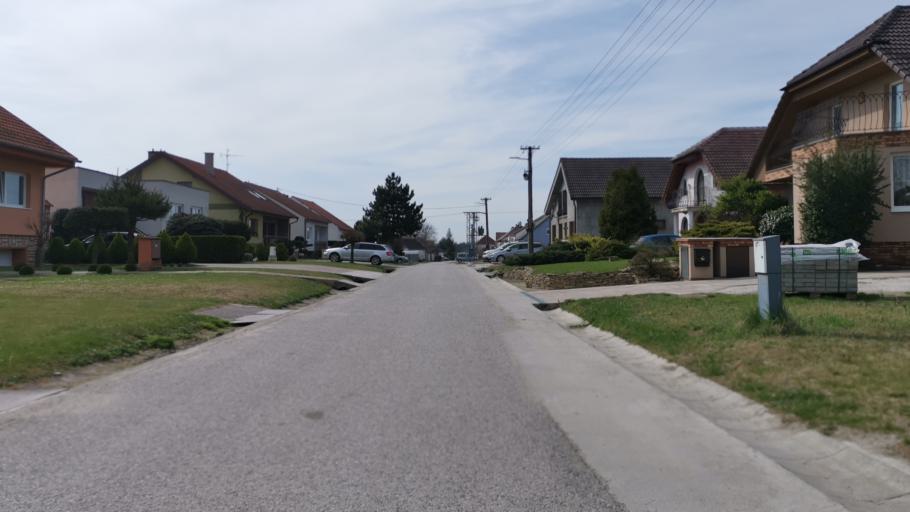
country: SK
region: Trnavsky
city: Gbely
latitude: 48.6571
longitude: 17.0863
